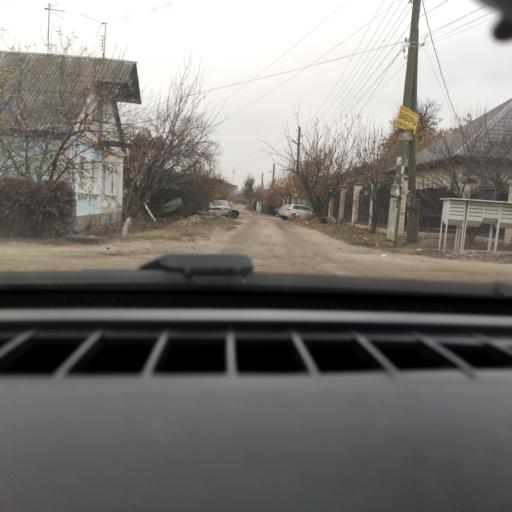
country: RU
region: Voronezj
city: Voronezh
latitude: 51.6665
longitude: 39.2895
